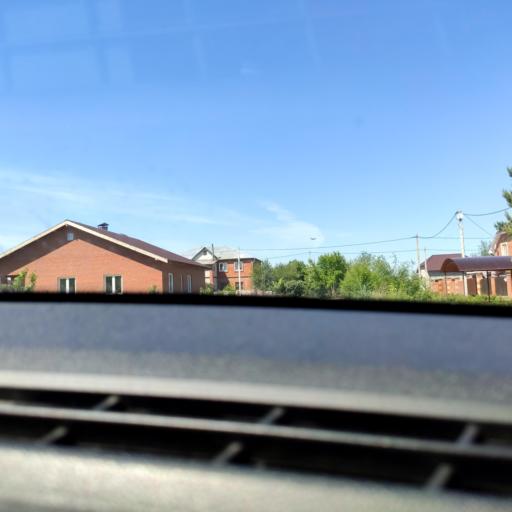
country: RU
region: Samara
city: Tol'yatti
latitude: 53.5584
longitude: 49.3820
